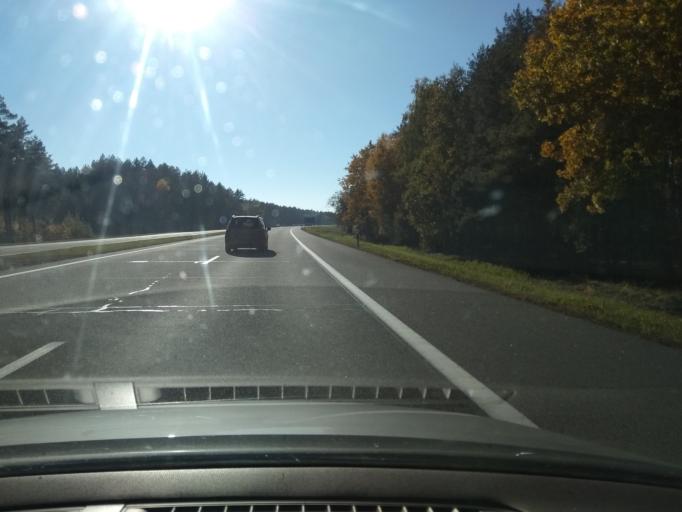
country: BY
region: Brest
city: Baranovichi
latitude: 53.0568
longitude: 25.8624
